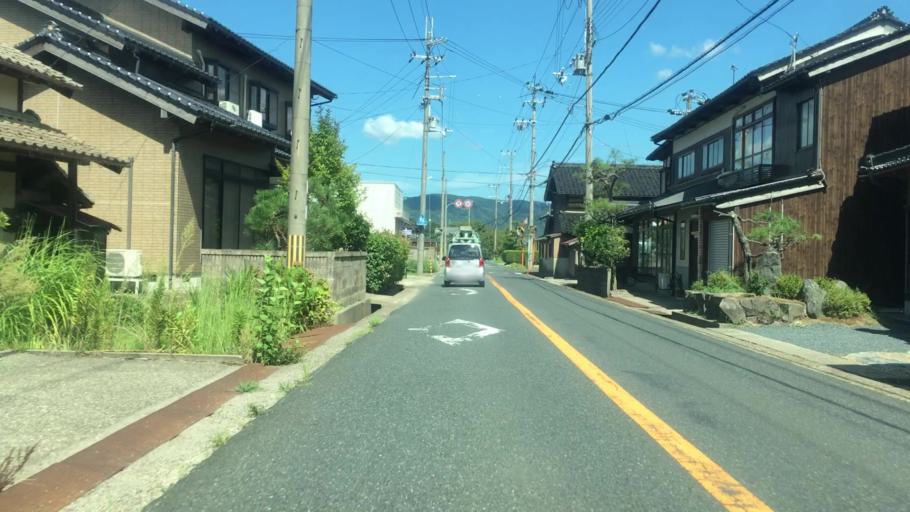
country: JP
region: Kyoto
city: Miyazu
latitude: 35.6089
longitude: 135.0508
